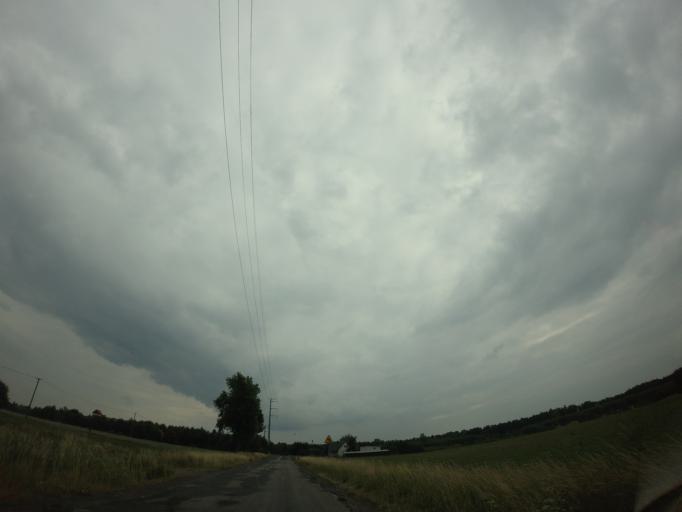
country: PL
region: West Pomeranian Voivodeship
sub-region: Powiat drawski
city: Czaplinek
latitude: 53.5151
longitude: 16.2242
